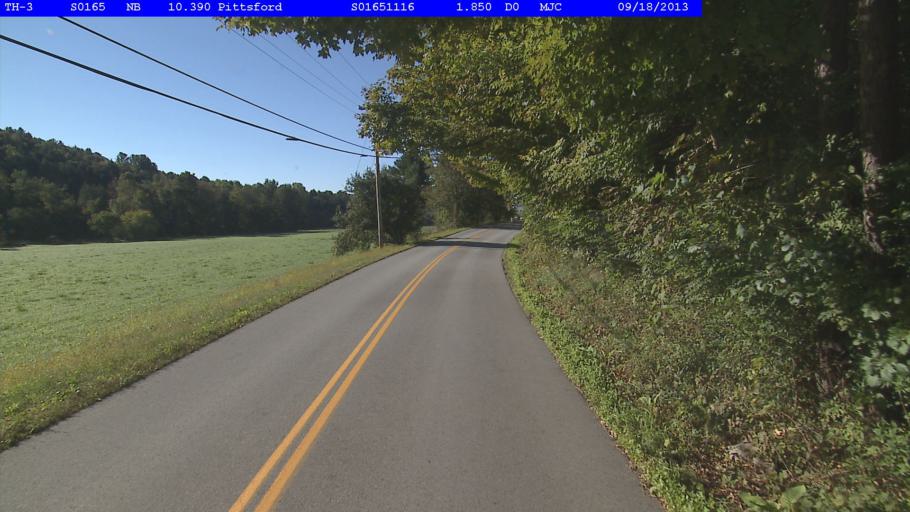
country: US
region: Vermont
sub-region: Rutland County
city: Rutland
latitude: 43.7158
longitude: -73.0064
